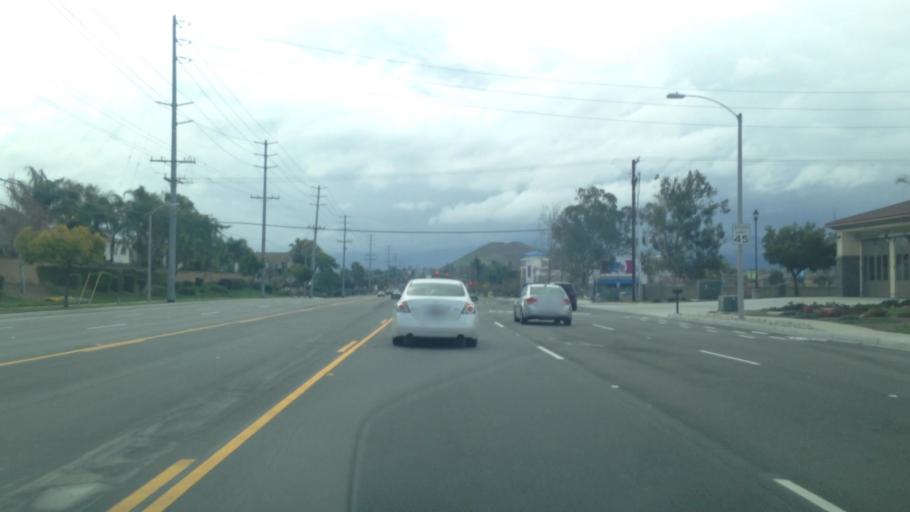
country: US
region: California
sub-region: Riverside County
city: Norco
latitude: 33.9599
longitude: -117.5584
